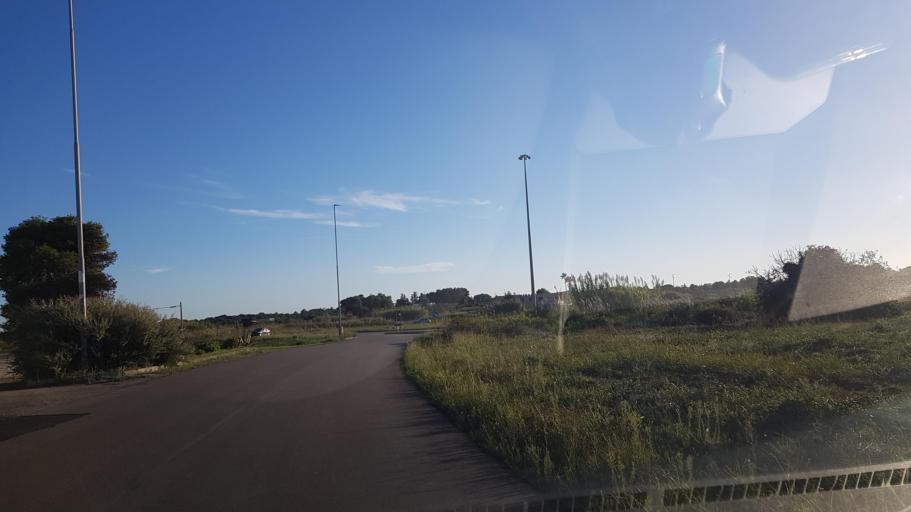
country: IT
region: Apulia
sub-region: Provincia di Lecce
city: Giorgilorio
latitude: 40.4575
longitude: 18.1948
